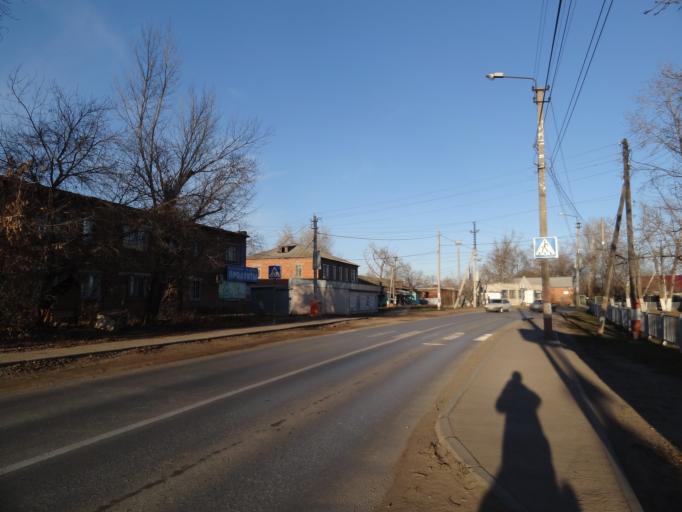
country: RU
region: Saratov
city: Engel's
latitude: 51.4976
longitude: 46.0599
